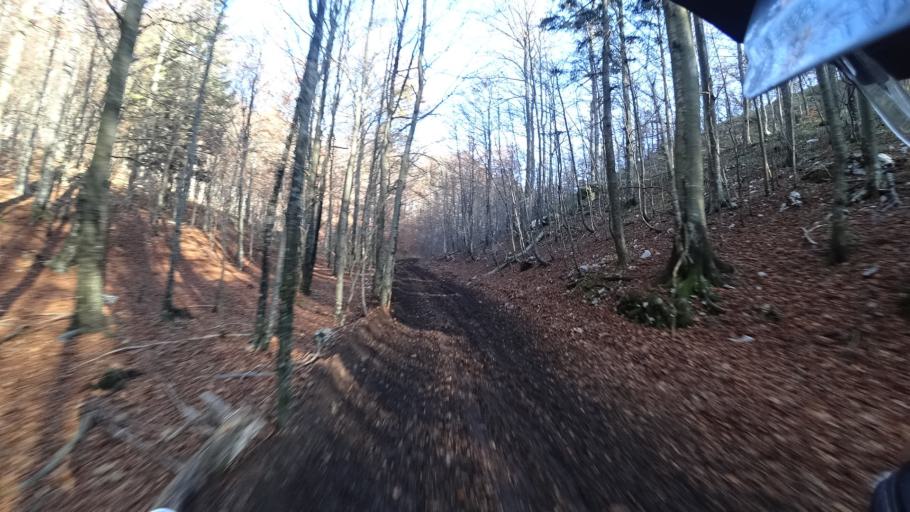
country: HR
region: Primorsko-Goranska
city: Klana
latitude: 45.4803
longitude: 14.4468
